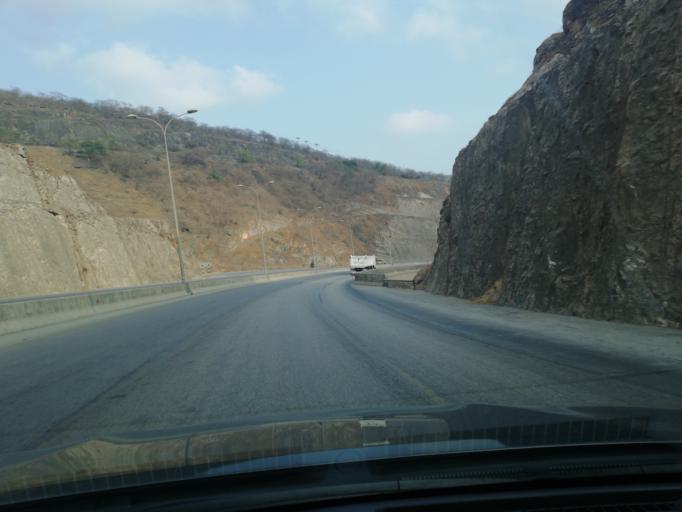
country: OM
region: Zufar
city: Salalah
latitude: 17.1396
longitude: 54.1336
